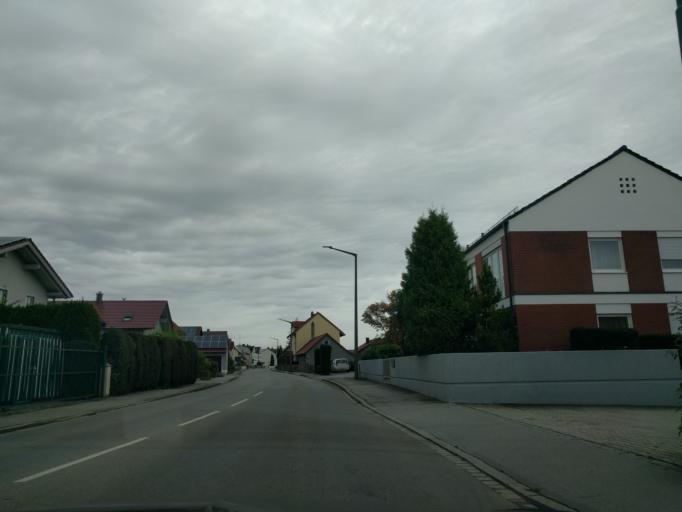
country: DE
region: Bavaria
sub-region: Lower Bavaria
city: Plattling
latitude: 48.7726
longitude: 12.8575
